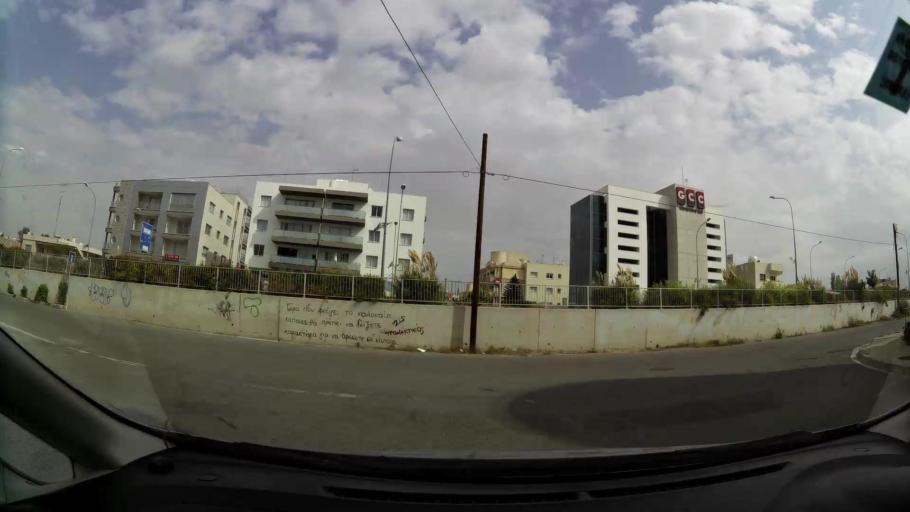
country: CY
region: Lefkosia
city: Geri
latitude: 35.1083
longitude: 33.3773
